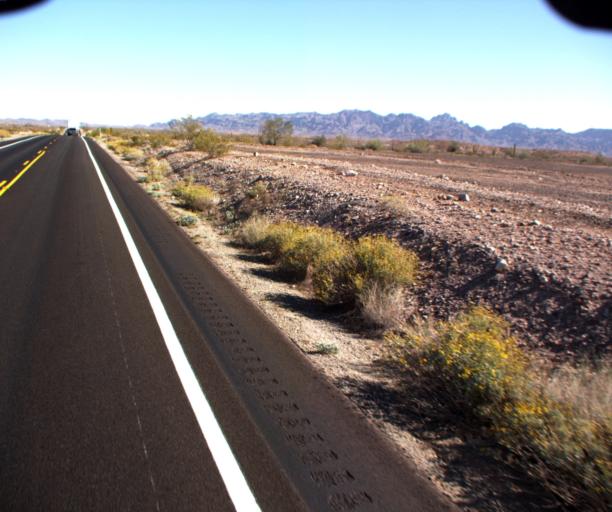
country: US
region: Arizona
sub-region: Yuma County
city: Wellton
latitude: 33.1118
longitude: -114.2949
